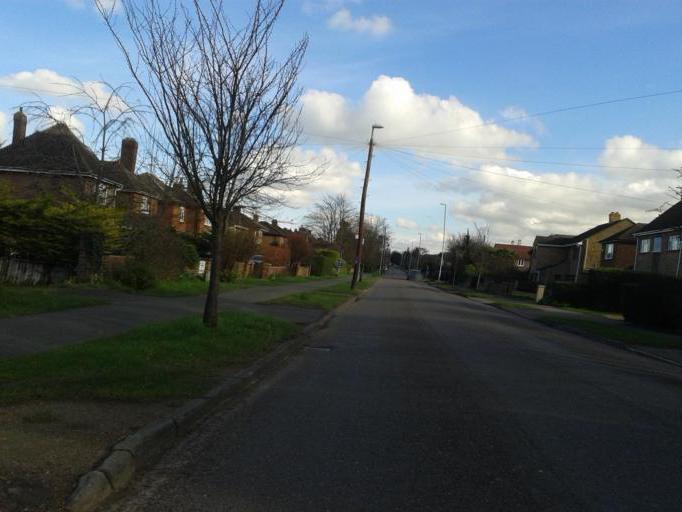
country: GB
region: England
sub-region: Cambridgeshire
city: Cambridge
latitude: 52.1797
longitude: 0.1537
